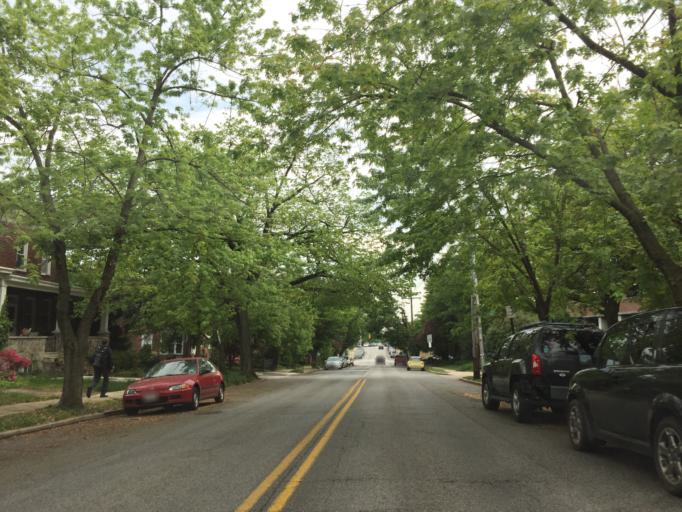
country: US
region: Maryland
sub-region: City of Baltimore
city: Baltimore
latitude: 39.3342
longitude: -76.6282
